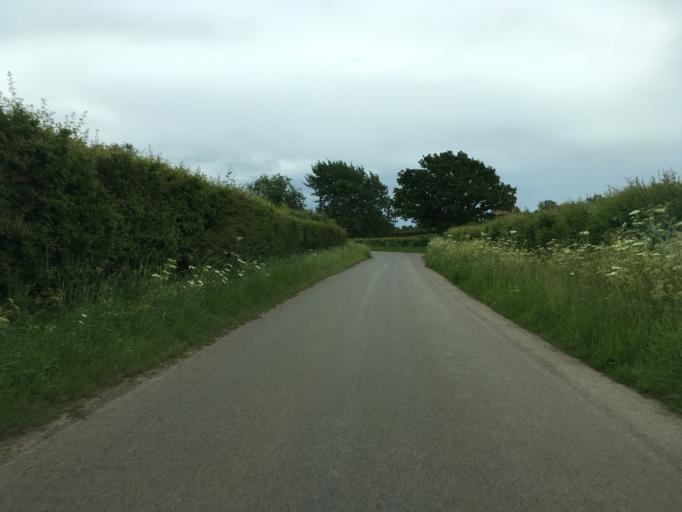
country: GB
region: England
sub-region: Wiltshire
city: Luckington
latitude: 51.5731
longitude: -2.2417
